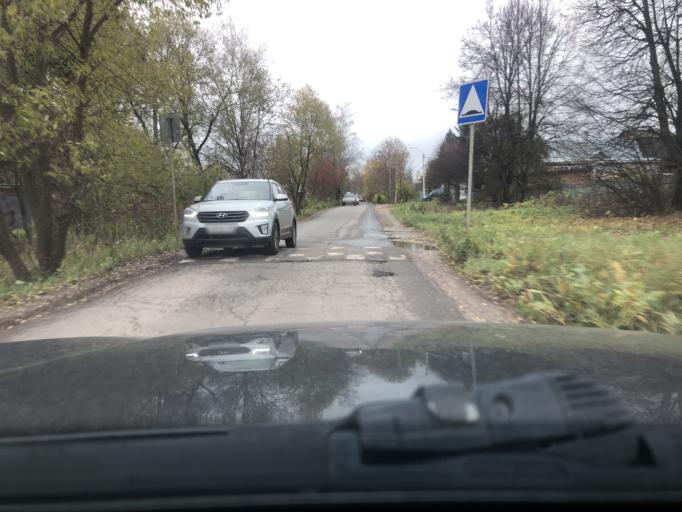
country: RU
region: Moskovskaya
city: Sergiyev Posad
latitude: 56.2969
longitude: 38.1122
